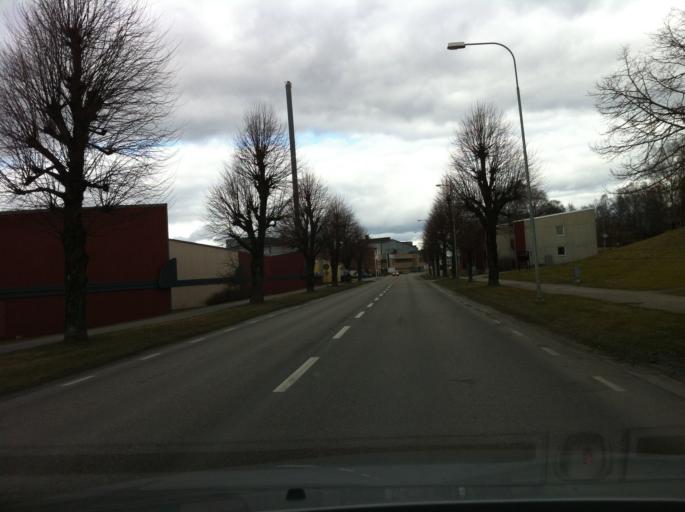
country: SE
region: Vaestra Goetaland
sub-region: Tranemo Kommun
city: Limmared
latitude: 57.5381
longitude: 13.3553
